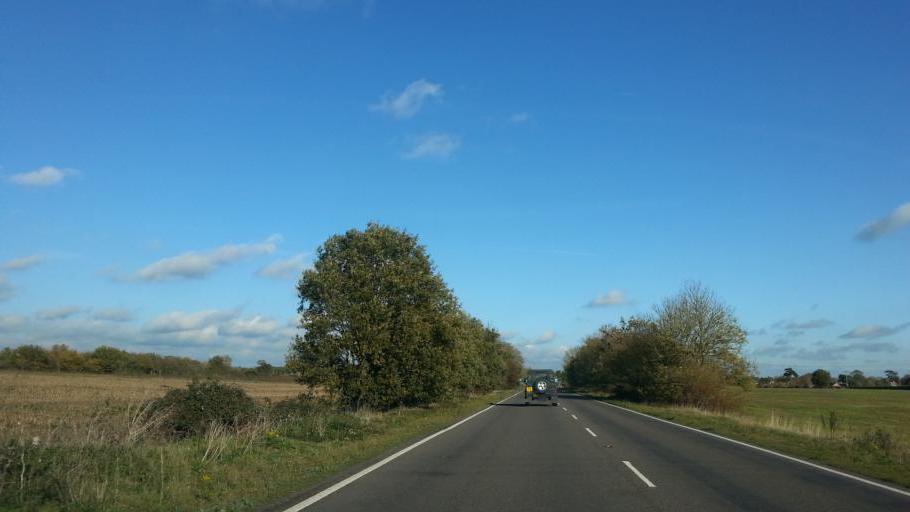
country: GB
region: England
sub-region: Suffolk
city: Bungay
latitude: 52.4465
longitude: 1.4058
